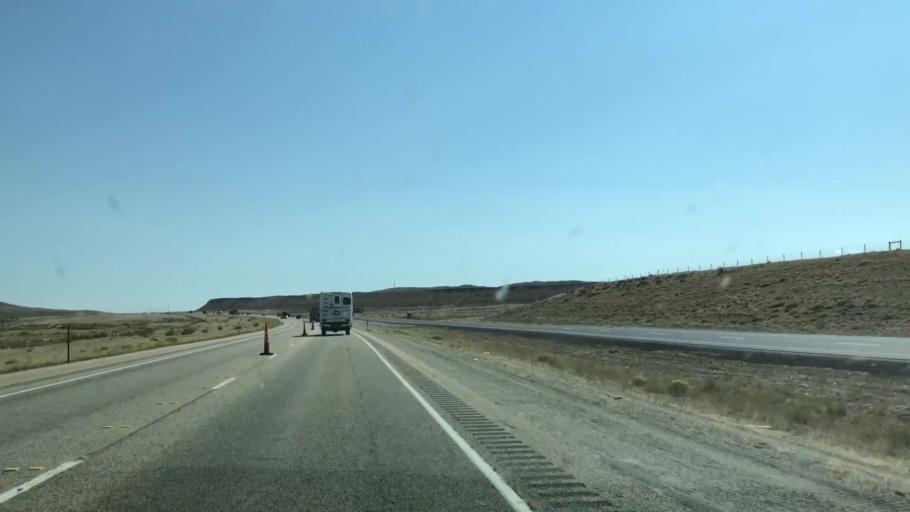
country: US
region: Wyoming
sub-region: Carbon County
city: Rawlins
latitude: 41.7449
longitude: -106.9306
